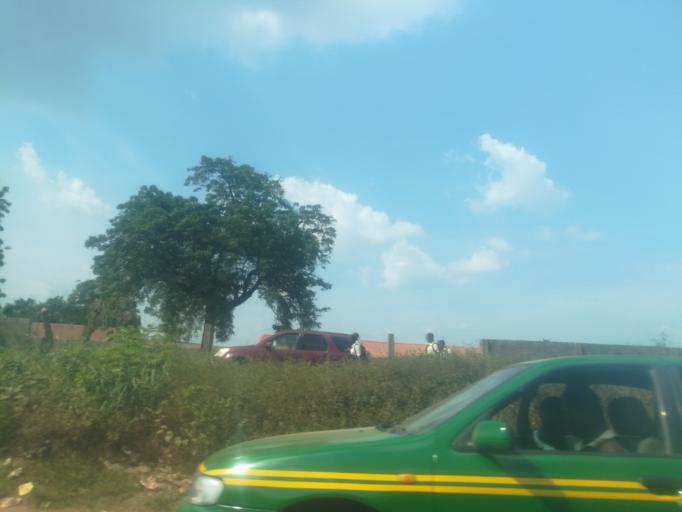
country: NG
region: Ogun
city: Abeokuta
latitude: 7.1720
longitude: 3.3700
